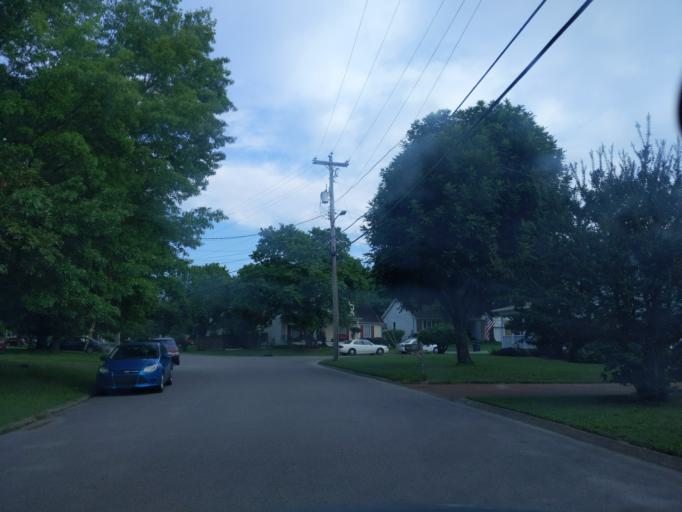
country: US
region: Tennessee
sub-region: Wilson County
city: Green Hill
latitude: 36.1847
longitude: -86.5992
